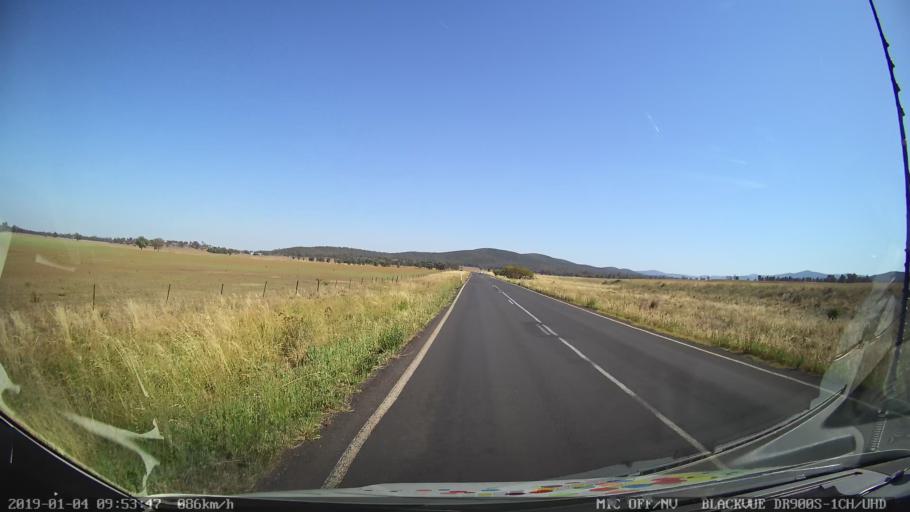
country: AU
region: New South Wales
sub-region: Cabonne
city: Canowindra
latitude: -33.5482
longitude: 148.4199
